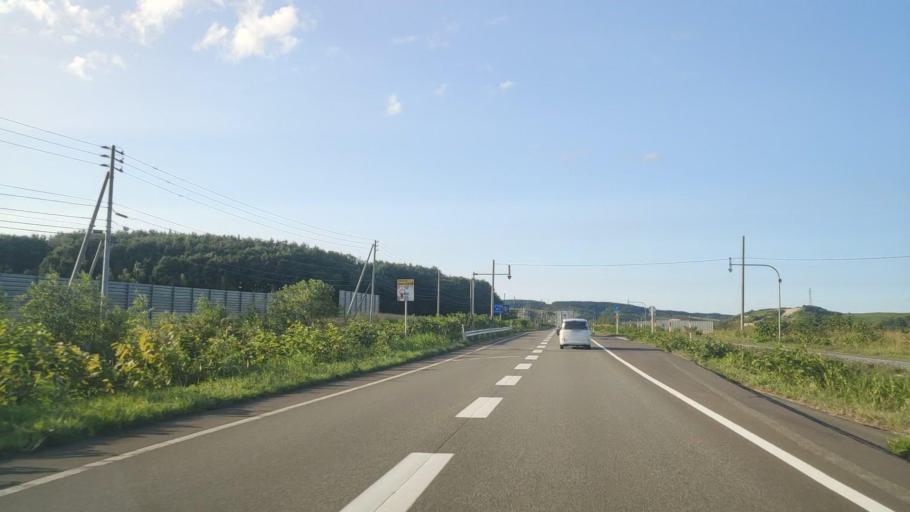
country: JP
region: Hokkaido
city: Wakkanai
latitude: 45.3232
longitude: 141.7195
